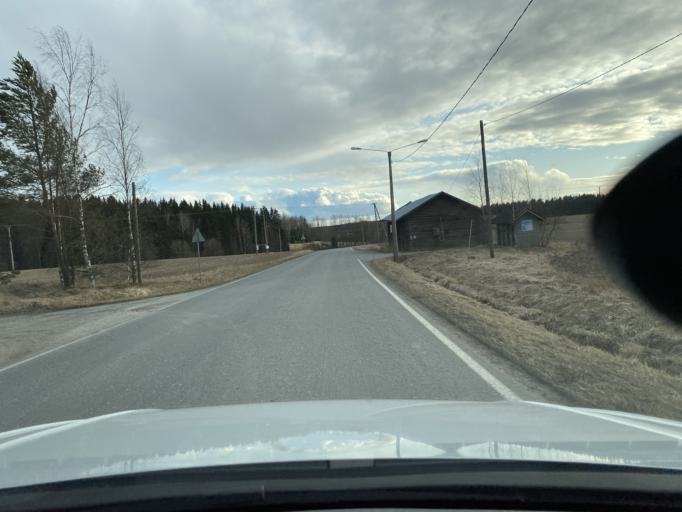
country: FI
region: Pirkanmaa
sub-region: Lounais-Pirkanmaa
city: Punkalaidun
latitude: 61.1649
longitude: 23.1876
